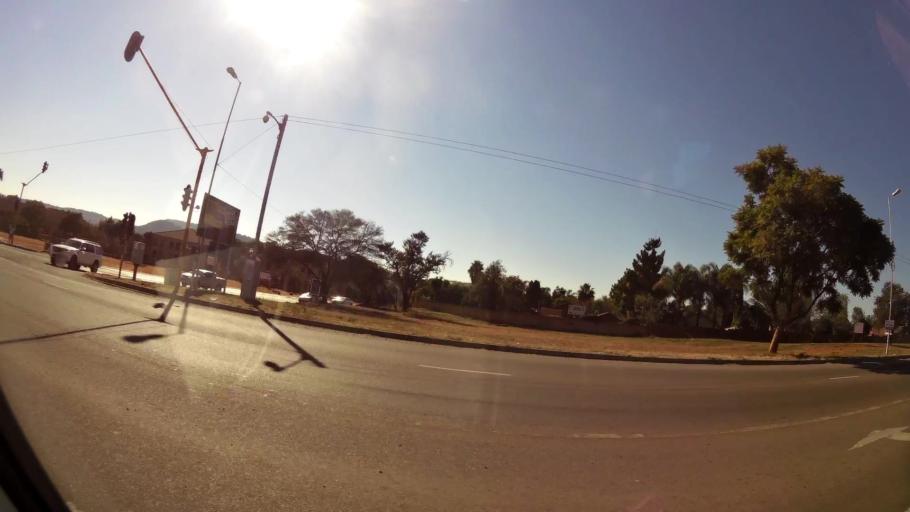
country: ZA
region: Gauteng
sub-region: City of Tshwane Metropolitan Municipality
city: Pretoria
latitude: -25.7913
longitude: 28.3108
